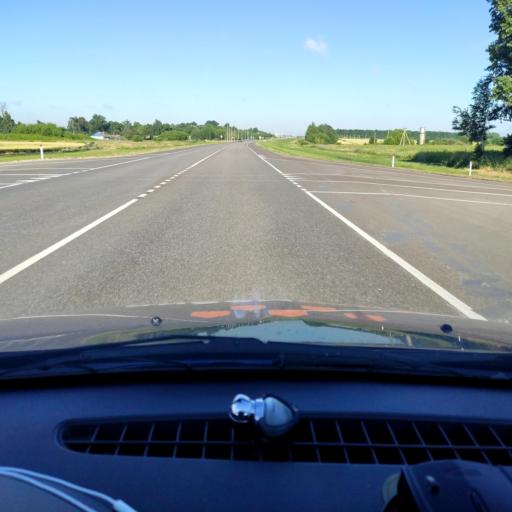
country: RU
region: Orjol
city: Pokrovskoye
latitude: 52.6229
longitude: 36.7931
